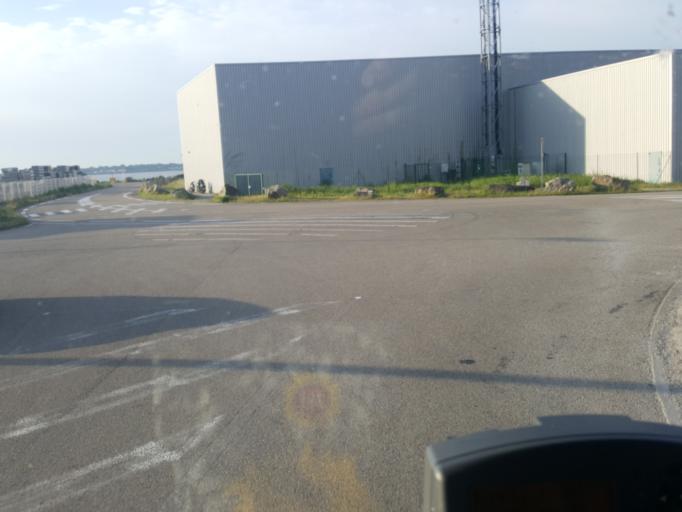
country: FR
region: Pays de la Loire
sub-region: Departement de la Loire-Atlantique
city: Saint-Nazaire
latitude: 47.2798
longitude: -2.1922
